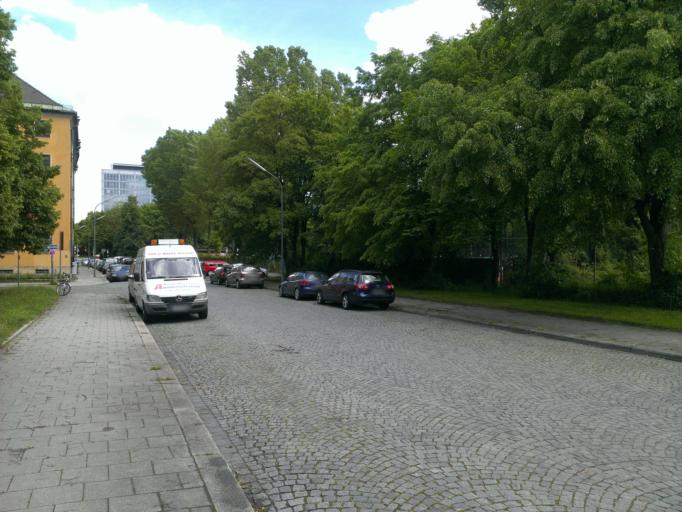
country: DE
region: Bavaria
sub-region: Upper Bavaria
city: Munich
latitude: 48.1676
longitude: 11.5330
